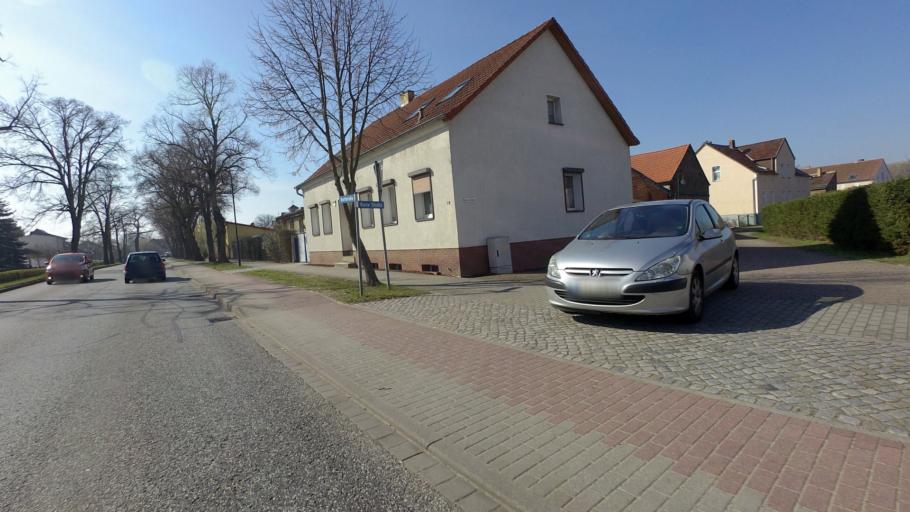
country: DE
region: Brandenburg
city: Rangsdorf
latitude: 52.2719
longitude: 13.4637
